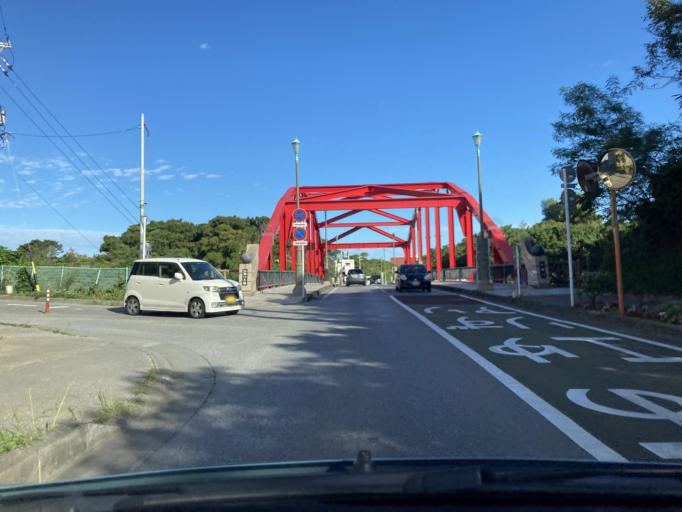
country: JP
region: Okinawa
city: Chatan
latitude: 26.3634
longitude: 127.7483
